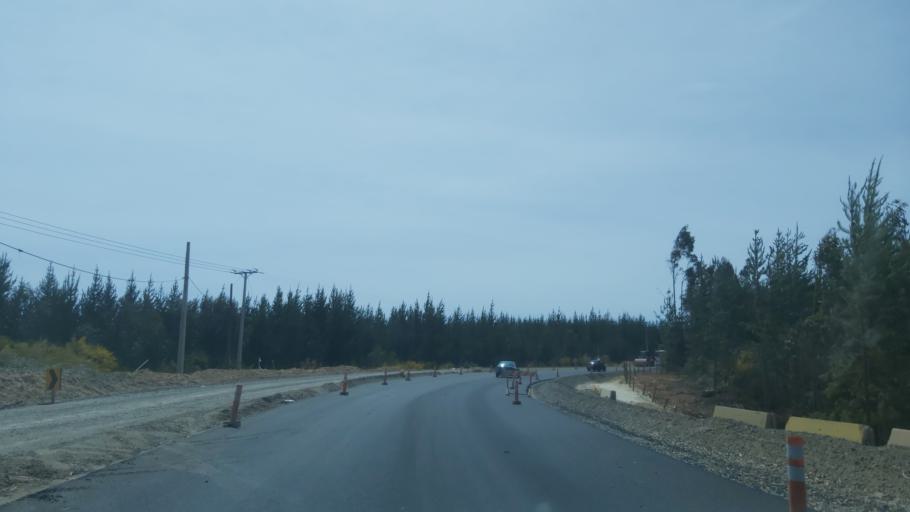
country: CL
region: Maule
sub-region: Provincia de Talca
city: Constitucion
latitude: -35.3839
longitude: -72.4204
